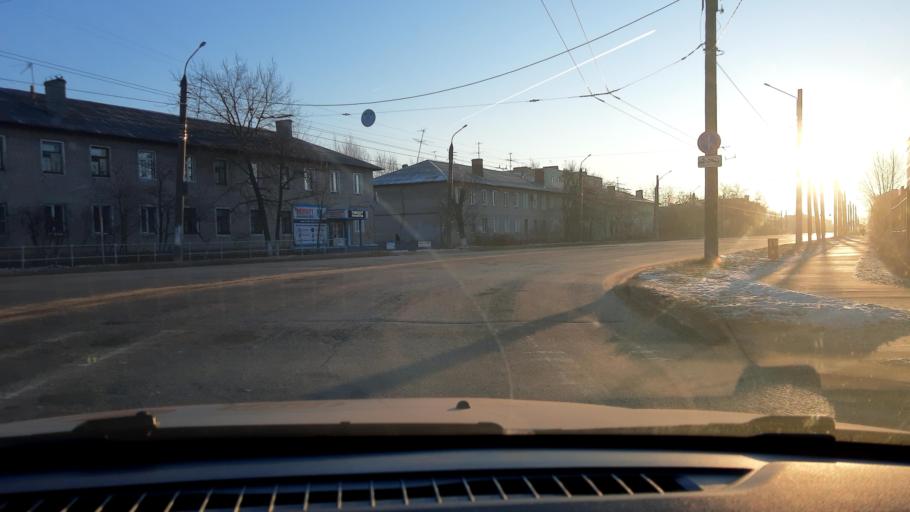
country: RU
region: Nizjnij Novgorod
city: Dzerzhinsk
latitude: 56.2473
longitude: 43.4746
